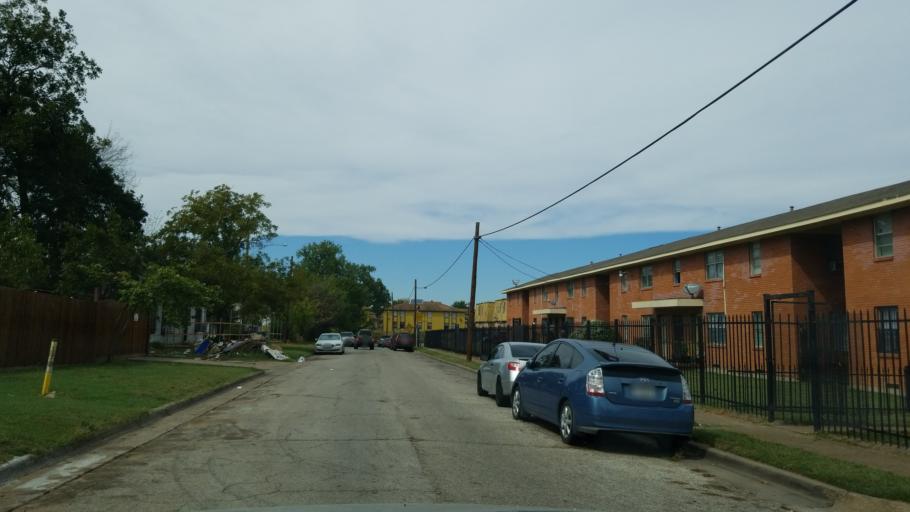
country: US
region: Texas
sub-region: Dallas County
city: Dallas
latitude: 32.7694
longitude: -96.7397
